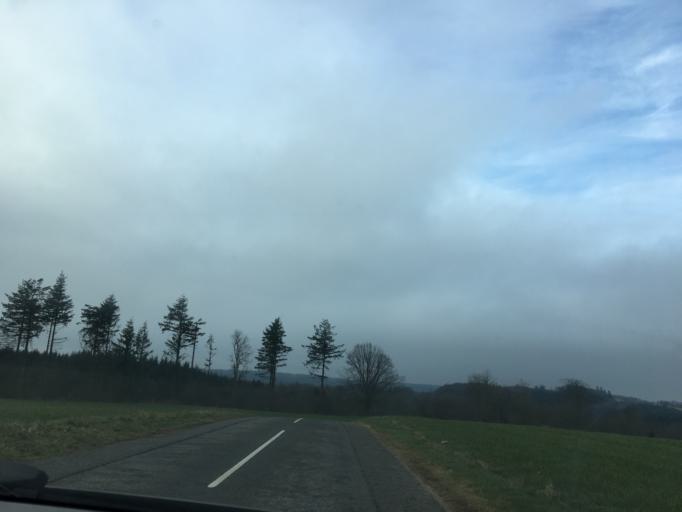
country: DK
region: South Denmark
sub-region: Vejle Kommune
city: Brejning
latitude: 55.7244
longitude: 9.6402
